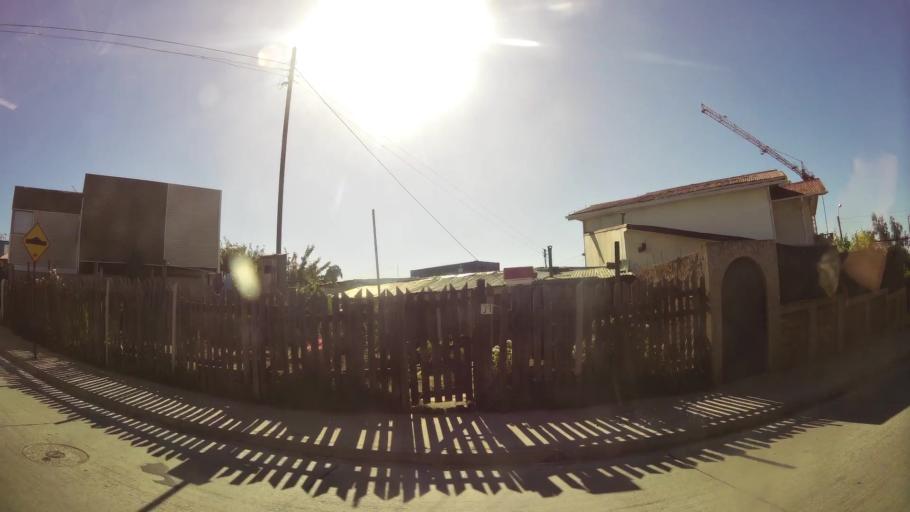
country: CL
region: Valparaiso
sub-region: Provincia de Valparaiso
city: Vina del Mar
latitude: -33.0427
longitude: -71.5558
